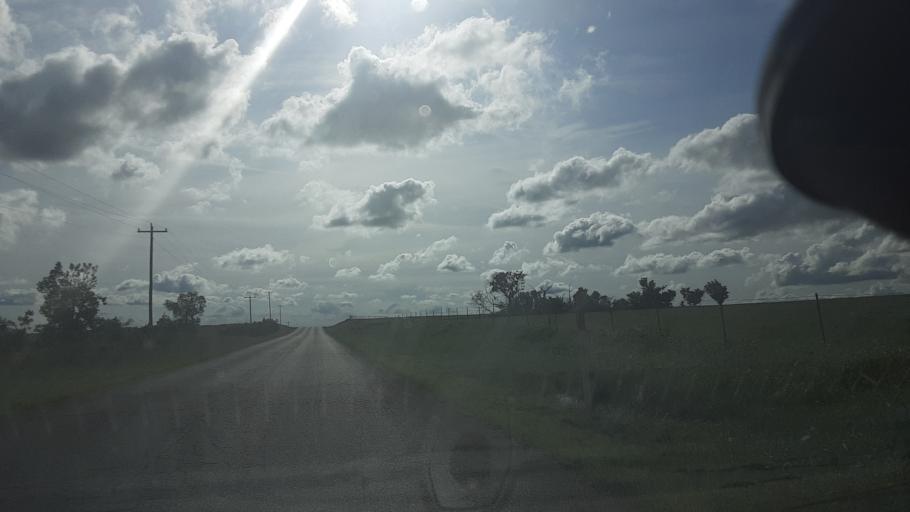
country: US
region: Oklahoma
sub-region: Logan County
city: Langston
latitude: 36.0578
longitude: -97.3543
